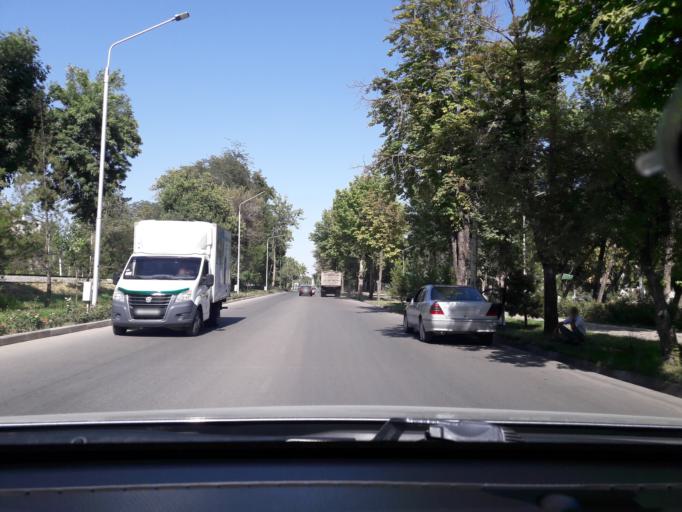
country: TJ
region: Dushanbe
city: Dushanbe
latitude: 38.5685
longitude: 68.7499
